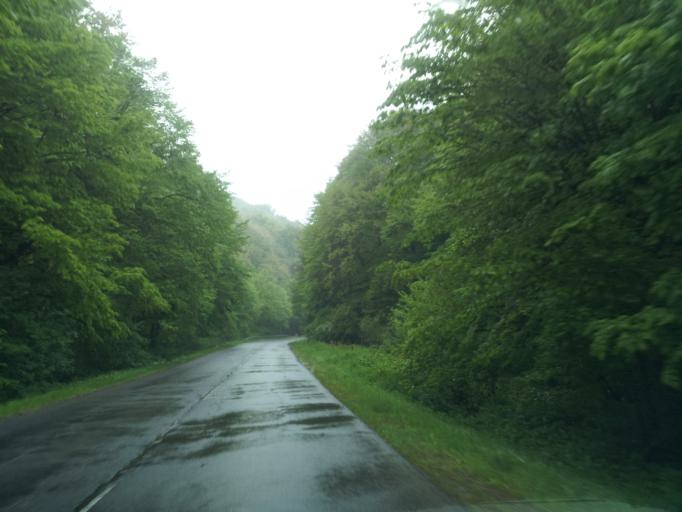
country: HU
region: Baranya
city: Komlo
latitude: 46.2029
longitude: 18.3006
